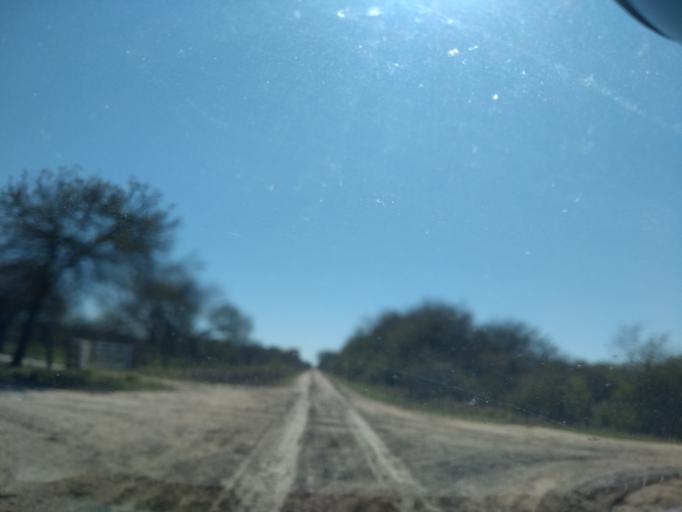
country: AR
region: Chaco
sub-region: Departamento de Quitilipi
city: Quitilipi
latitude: -26.7302
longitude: -60.2315
